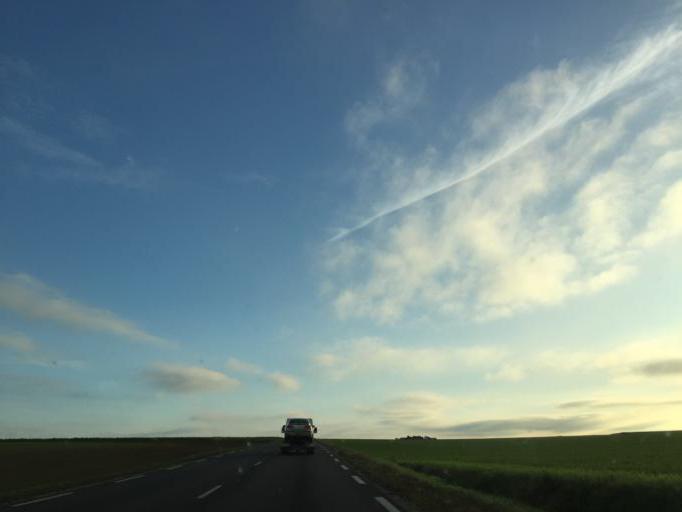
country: FR
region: Bourgogne
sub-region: Departement de l'Yonne
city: Sergines
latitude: 48.3653
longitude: 3.2329
